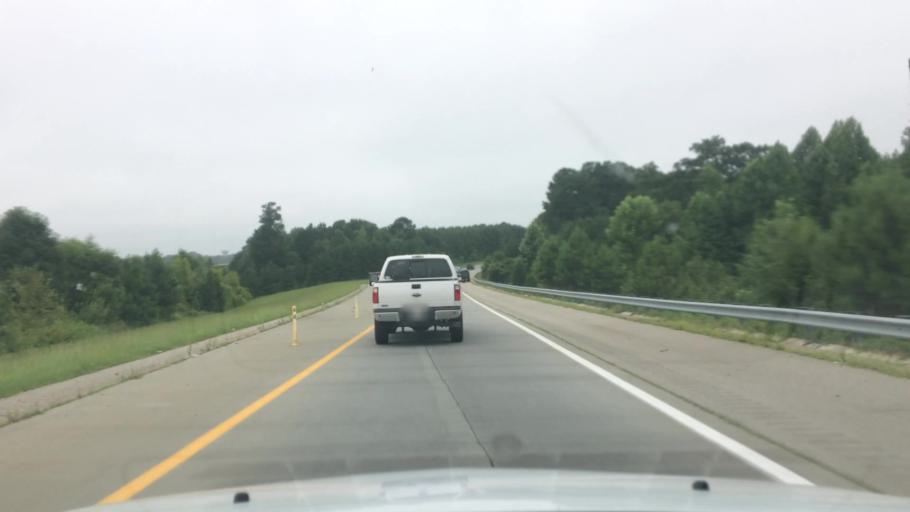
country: US
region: North Carolina
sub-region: Wake County
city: Knightdale
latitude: 35.7678
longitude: -78.4989
